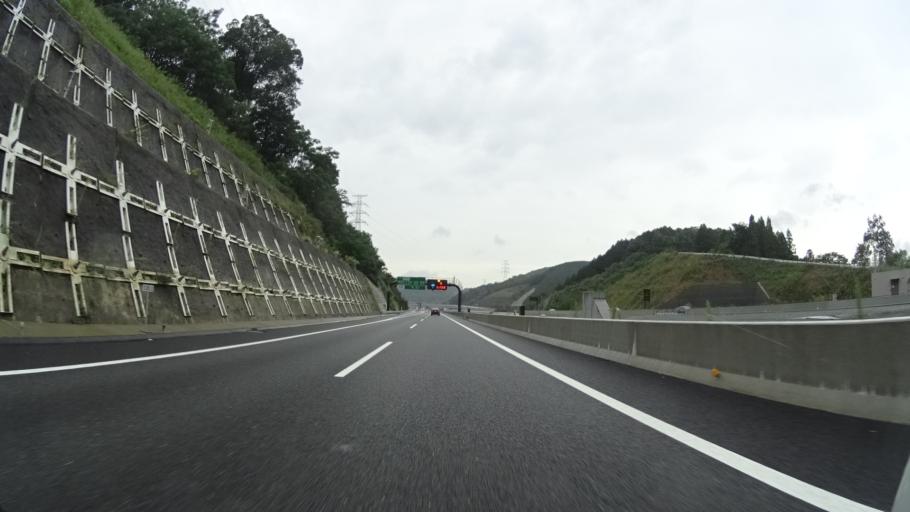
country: JP
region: Osaka
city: Mino
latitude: 34.8769
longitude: 135.4622
